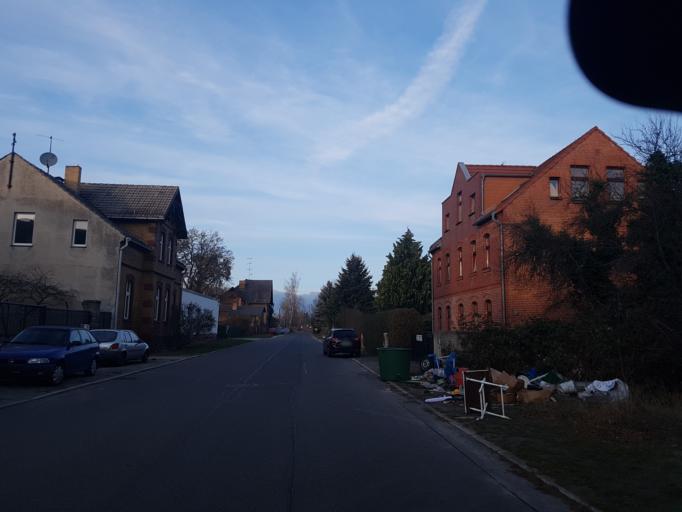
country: DE
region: Brandenburg
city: Finsterwalde
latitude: 51.6382
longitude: 13.7187
